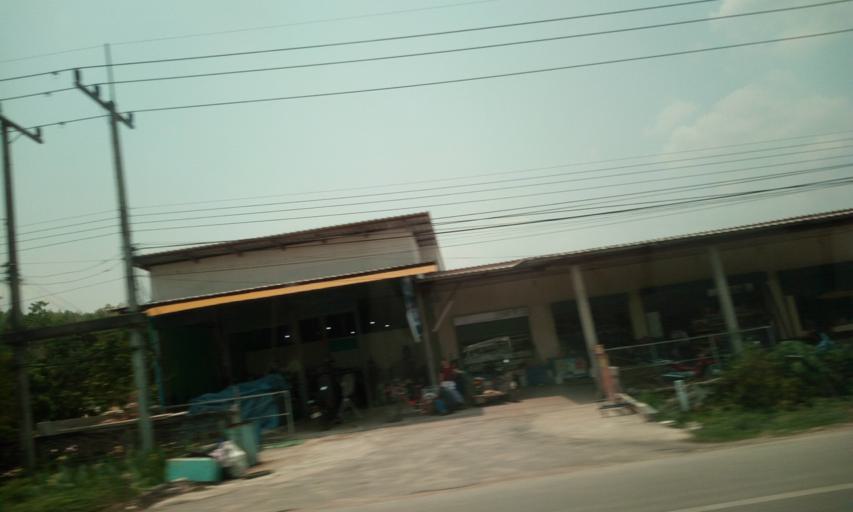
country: TH
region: Chiang Rai
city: Thoeng
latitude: 19.6885
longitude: 100.1400
